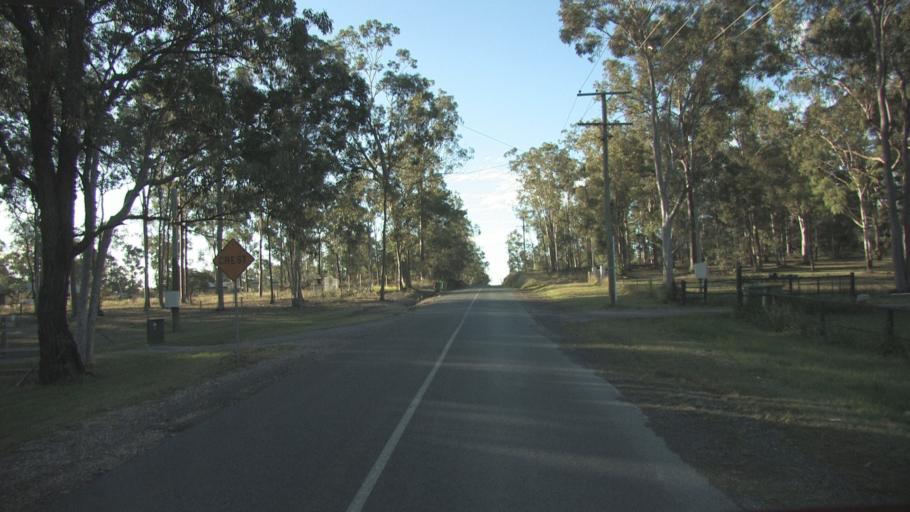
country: AU
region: Queensland
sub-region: Logan
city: Waterford West
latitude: -27.7267
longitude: 153.1471
